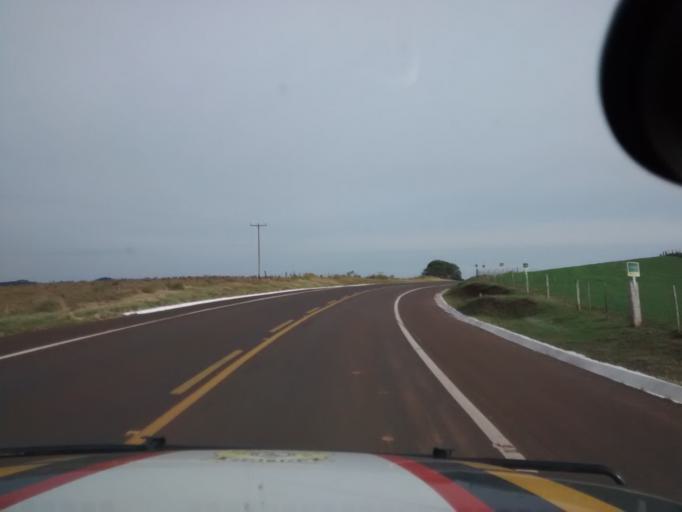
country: BR
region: Rio Grande do Sul
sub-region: Lagoa Vermelha
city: Lagoa Vermelha
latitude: -28.3330
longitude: -51.3175
